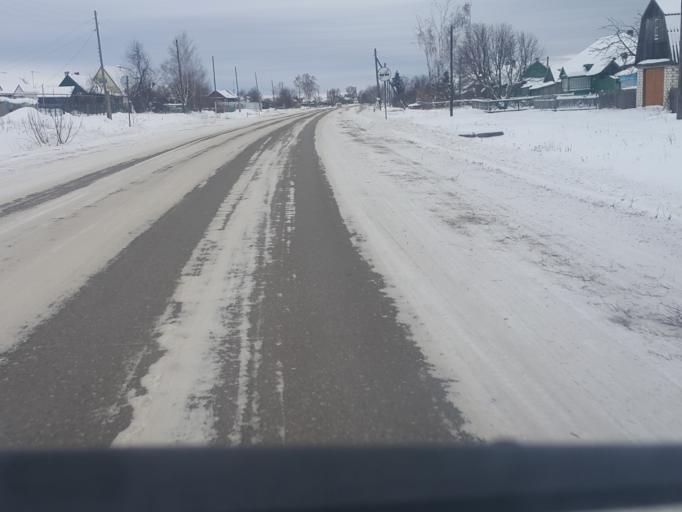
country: RU
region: Tambov
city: Platonovka
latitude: 52.8371
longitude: 41.8133
